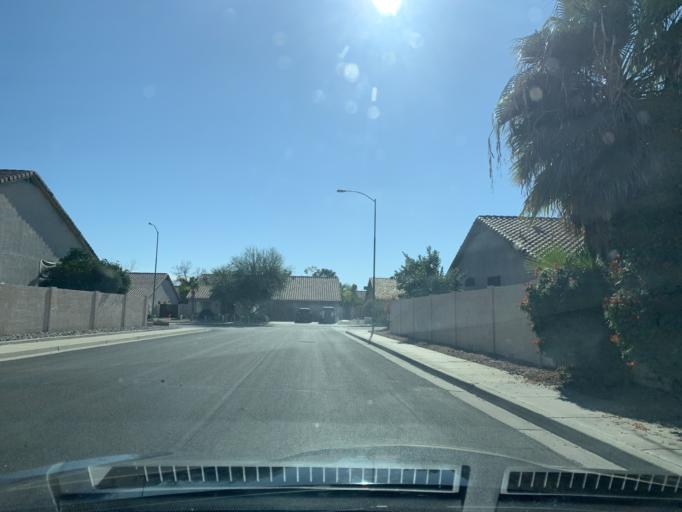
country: US
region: Arizona
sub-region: Pinal County
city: Apache Junction
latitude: 33.3824
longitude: -111.6268
